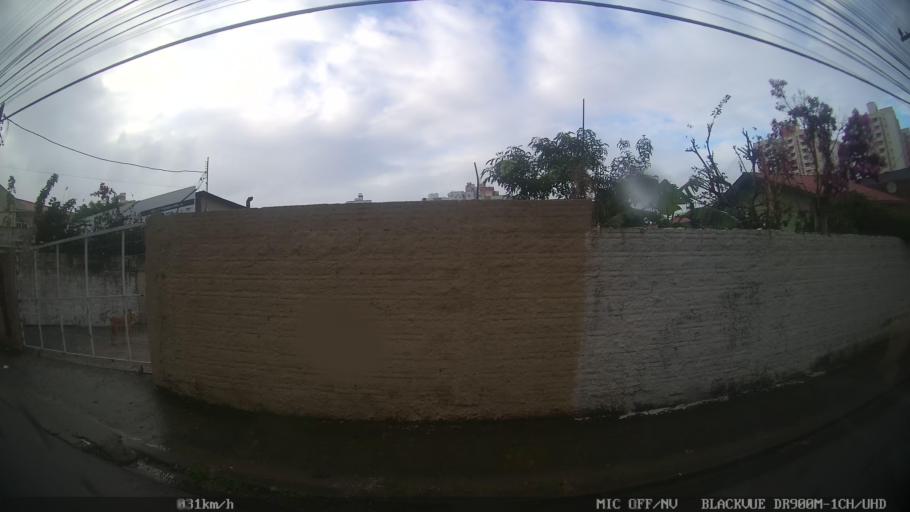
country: BR
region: Santa Catarina
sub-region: Sao Jose
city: Campinas
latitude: -27.5774
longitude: -48.6111
